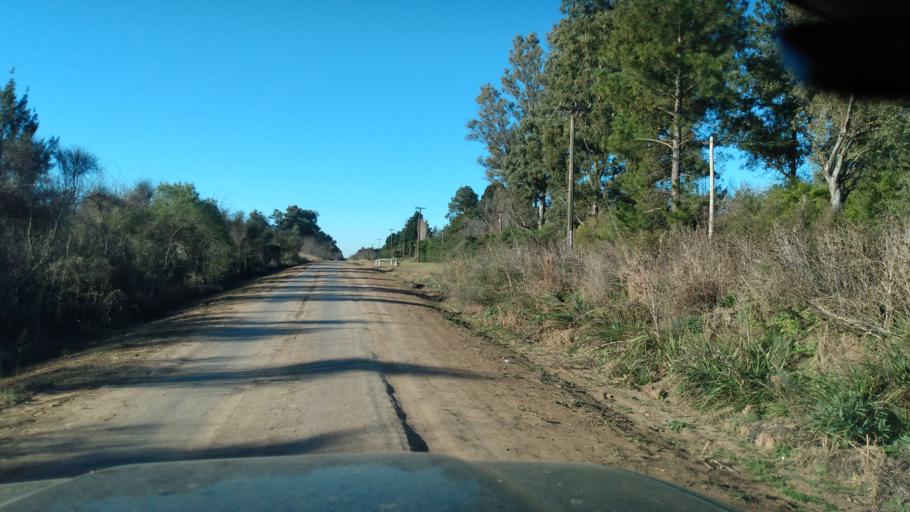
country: AR
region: Buenos Aires
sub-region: Partido de Lujan
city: Lujan
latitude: -34.5610
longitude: -59.1616
